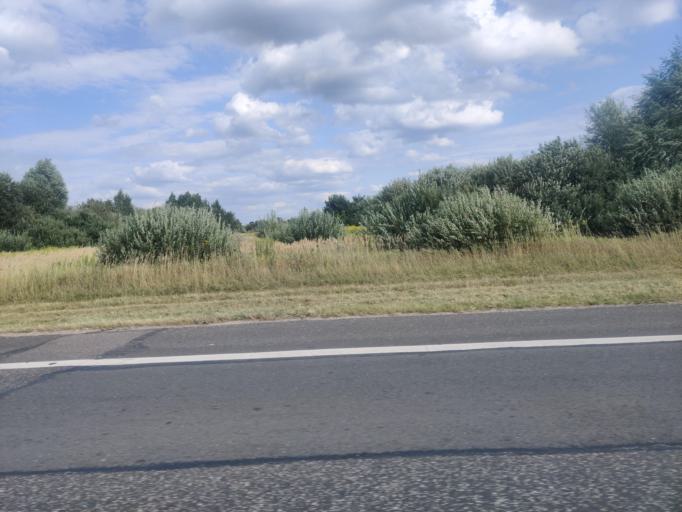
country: PL
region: Greater Poland Voivodeship
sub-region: Konin
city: Konin
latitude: 52.1967
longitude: 18.2682
